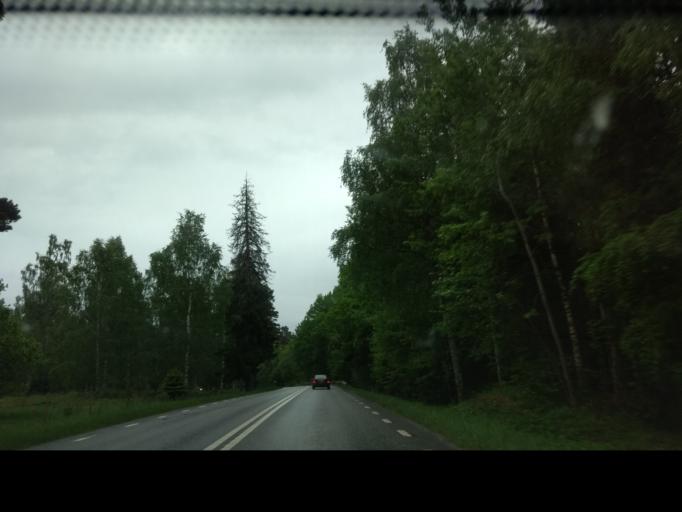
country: SE
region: Uppsala
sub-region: Uppsala Kommun
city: Saevja
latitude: 59.7599
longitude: 17.6458
